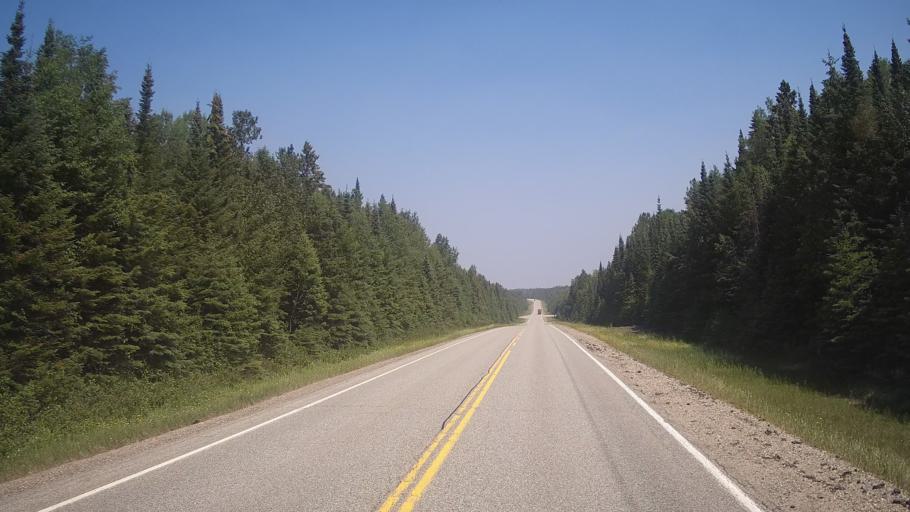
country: CA
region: Ontario
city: Timmins
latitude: 48.0886
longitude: -81.5950
